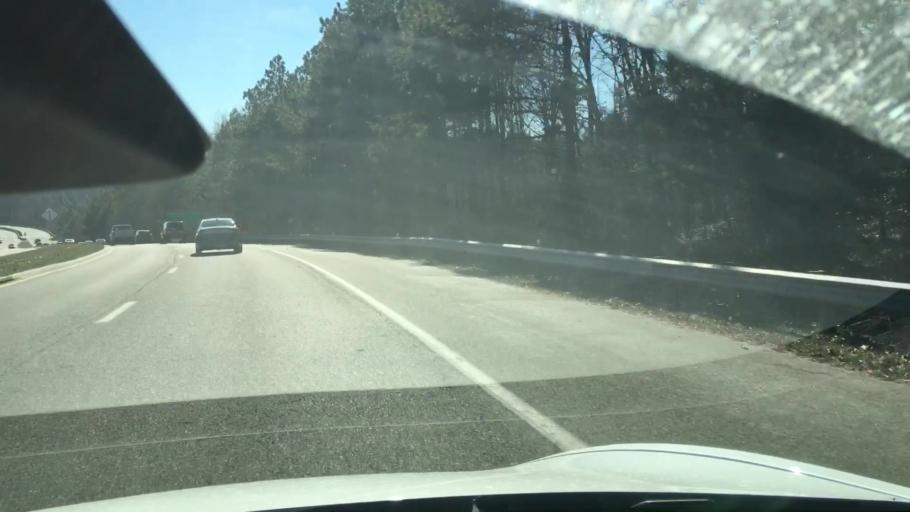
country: US
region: Virginia
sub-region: Henrico County
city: Tuckahoe
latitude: 37.5702
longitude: -77.5776
